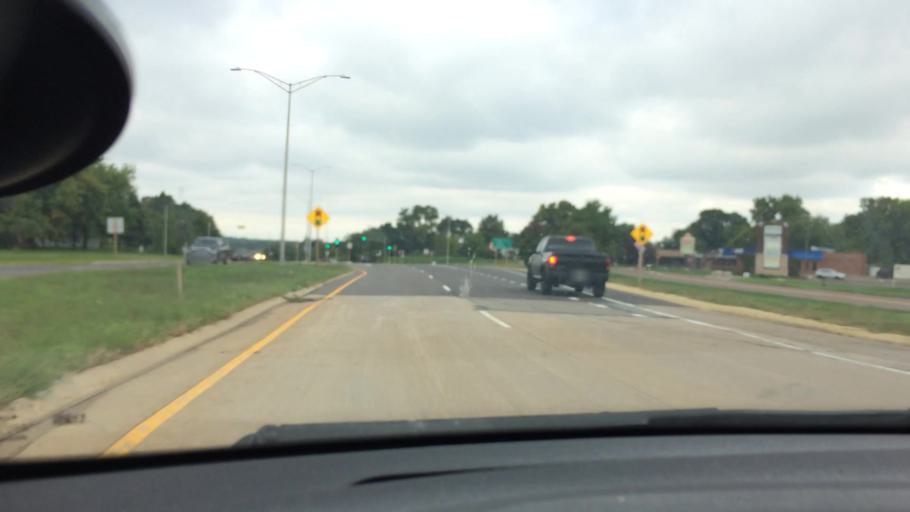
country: US
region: Wisconsin
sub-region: Chippewa County
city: Chippewa Falls
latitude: 44.9244
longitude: -91.3823
